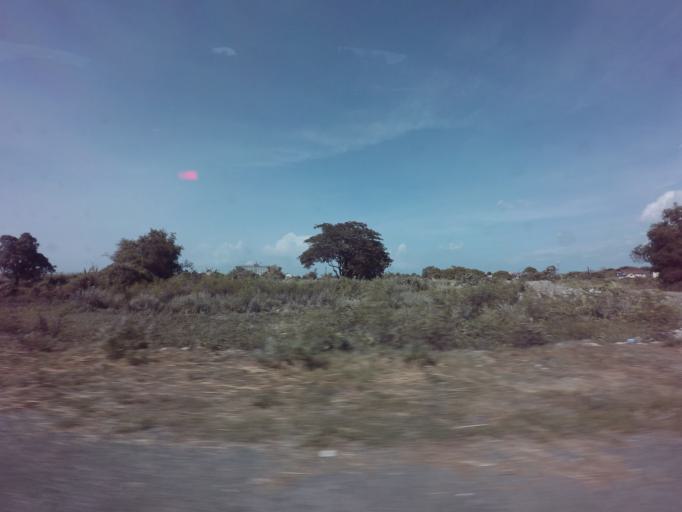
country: PH
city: Sambayanihan People's Village
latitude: 14.4733
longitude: 120.9856
